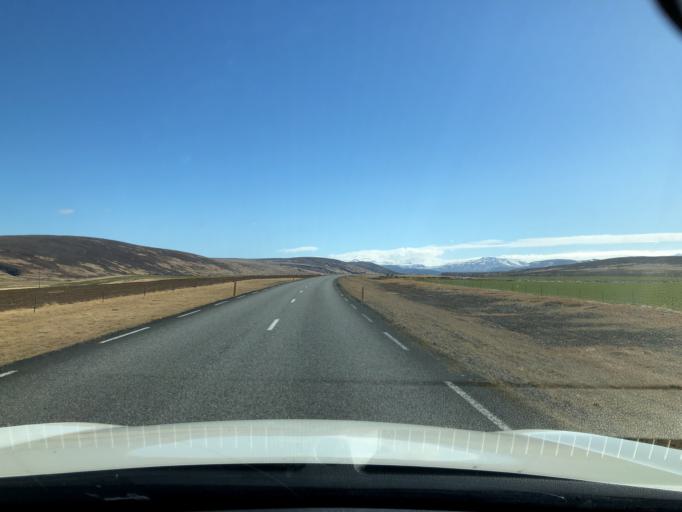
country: IS
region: South
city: Hveragerdi
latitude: 64.7010
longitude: -21.2168
